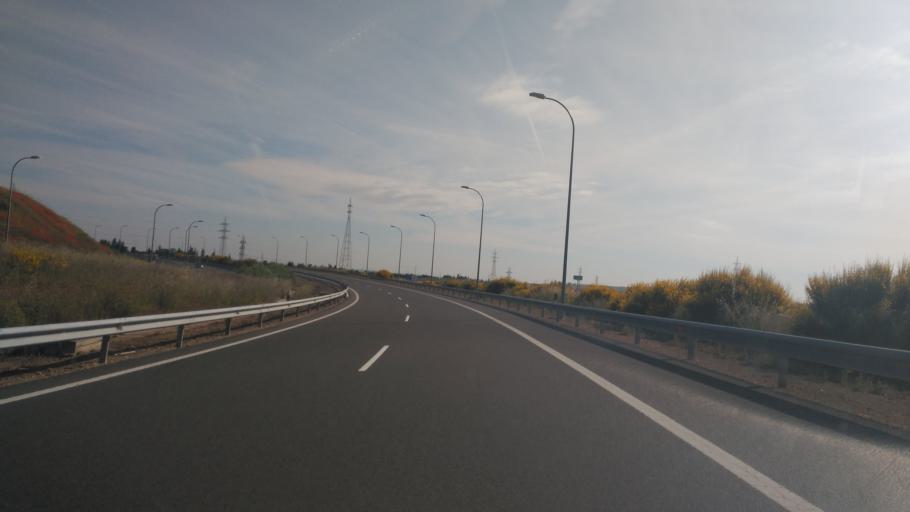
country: ES
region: Castille and Leon
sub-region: Provincia de Salamanca
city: Villamayor
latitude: 40.9932
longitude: -5.6756
